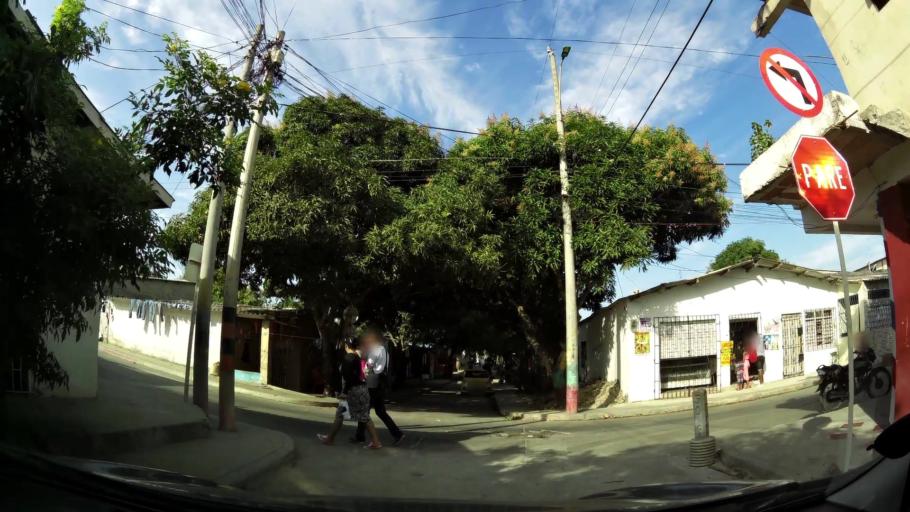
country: CO
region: Atlantico
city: Soledad
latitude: 10.9241
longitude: -74.8128
